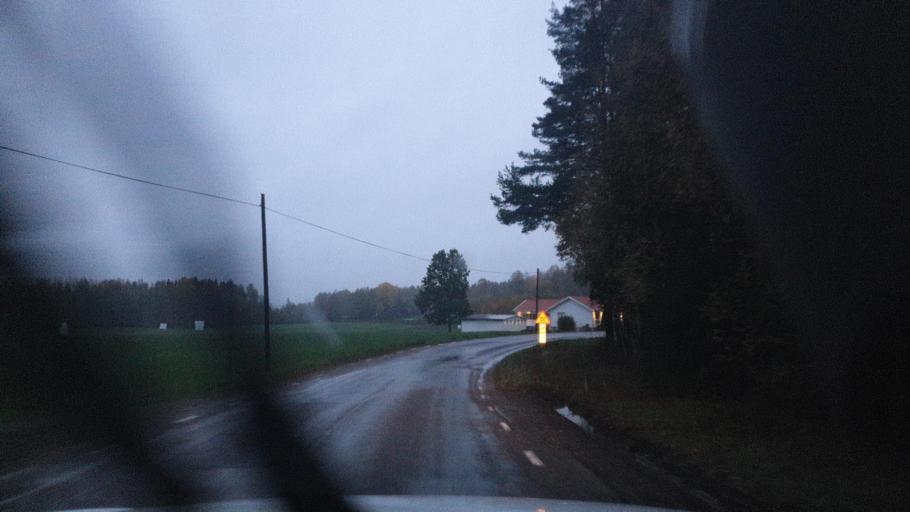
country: SE
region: Vaermland
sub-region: Eda Kommun
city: Charlottenberg
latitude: 59.8588
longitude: 12.3444
